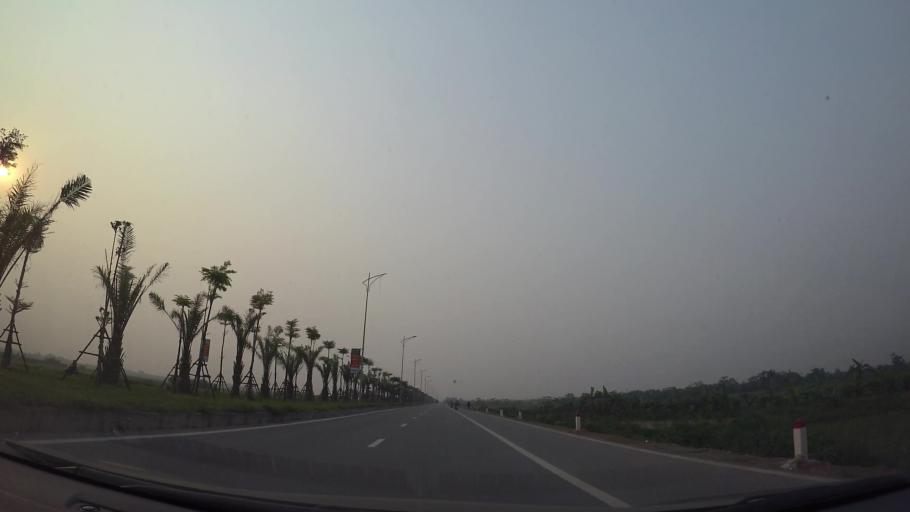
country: VN
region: Ha Noi
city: Kim Bai
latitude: 20.8744
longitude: 105.8026
